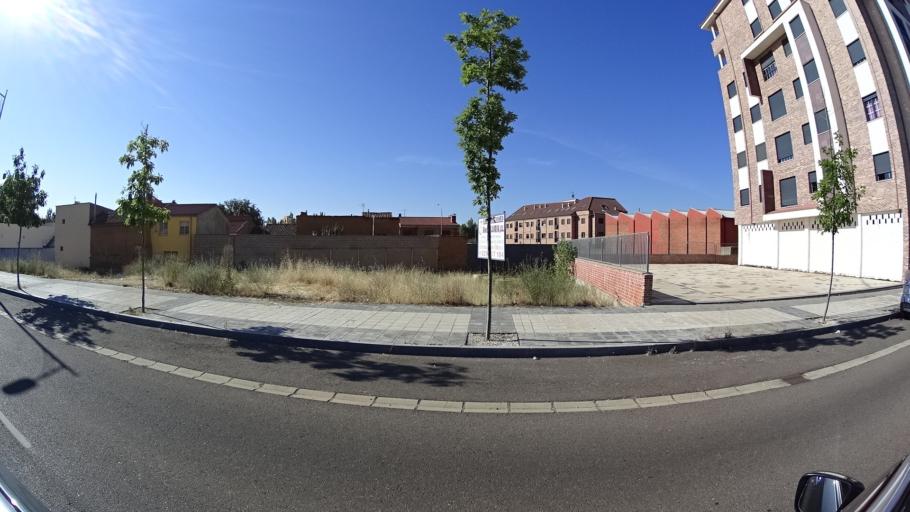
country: ES
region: Castille and Leon
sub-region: Provincia de Leon
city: Leon
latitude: 42.5828
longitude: -5.5582
